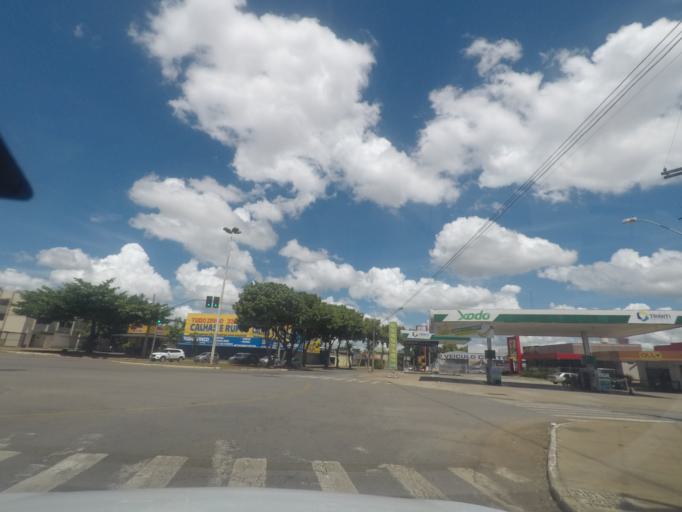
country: BR
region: Goias
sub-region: Goiania
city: Goiania
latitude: -16.6910
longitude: -49.3024
